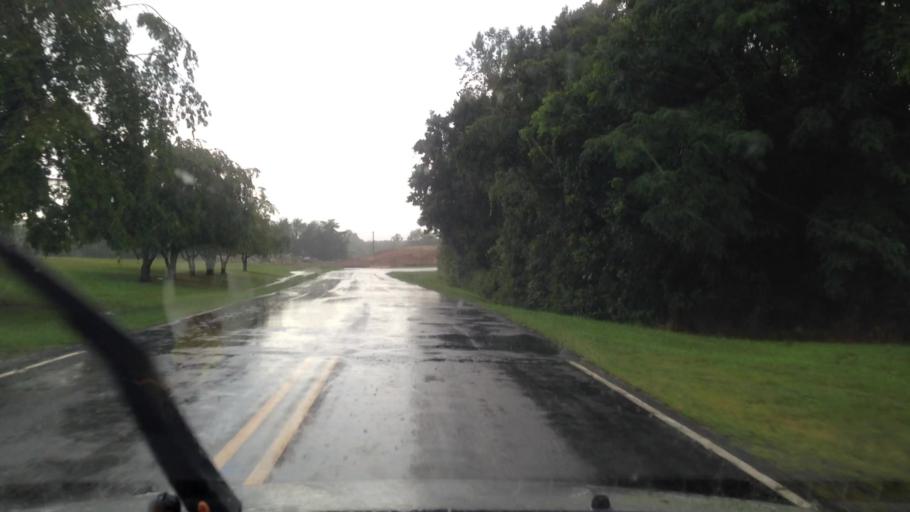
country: US
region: North Carolina
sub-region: Guilford County
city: Oak Ridge
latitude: 36.2103
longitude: -80.0273
